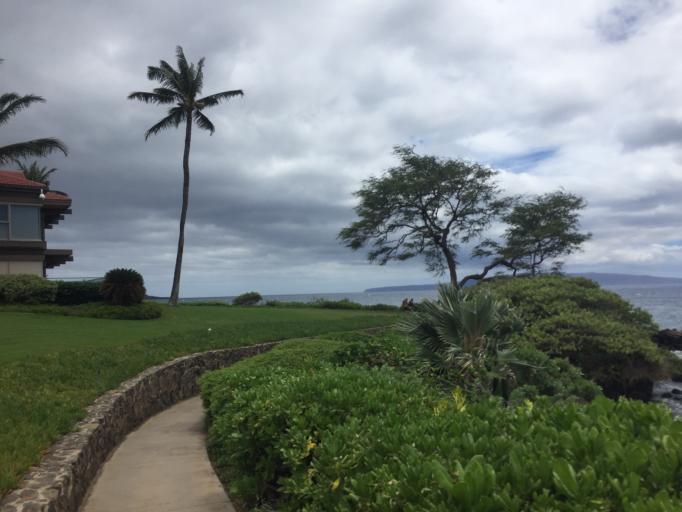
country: US
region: Hawaii
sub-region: Maui County
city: Kihei
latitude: 20.6802
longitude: -156.4447
